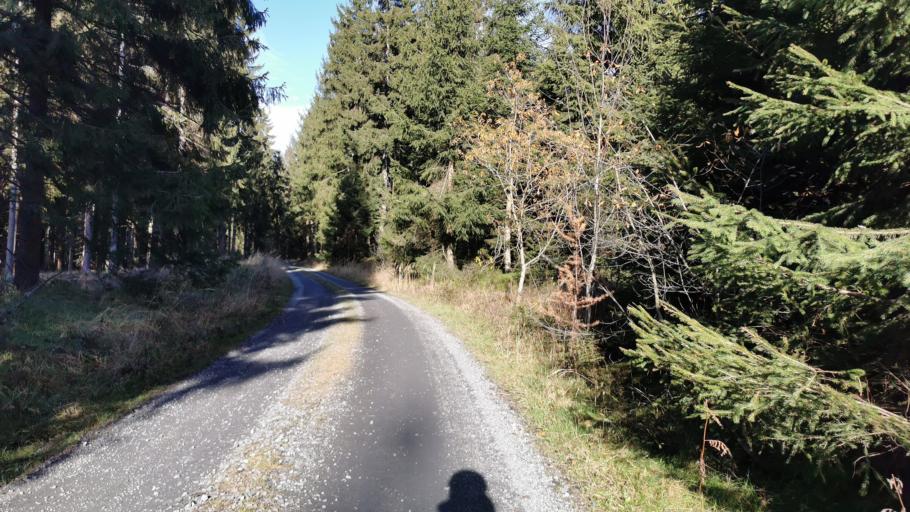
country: DE
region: Bavaria
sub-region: Upper Franconia
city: Reichenbach
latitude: 50.4338
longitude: 11.4377
